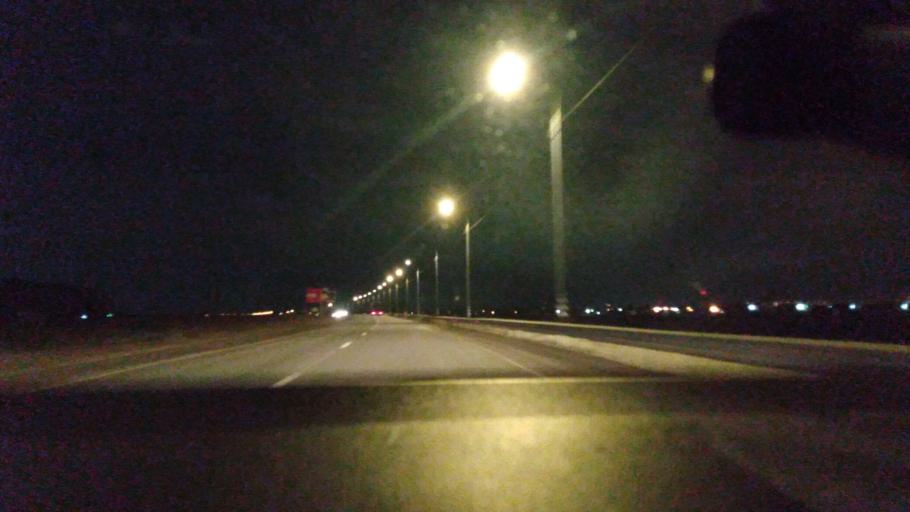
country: RU
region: Moskovskaya
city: Yegor'yevsk
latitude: 55.4006
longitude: 39.0603
